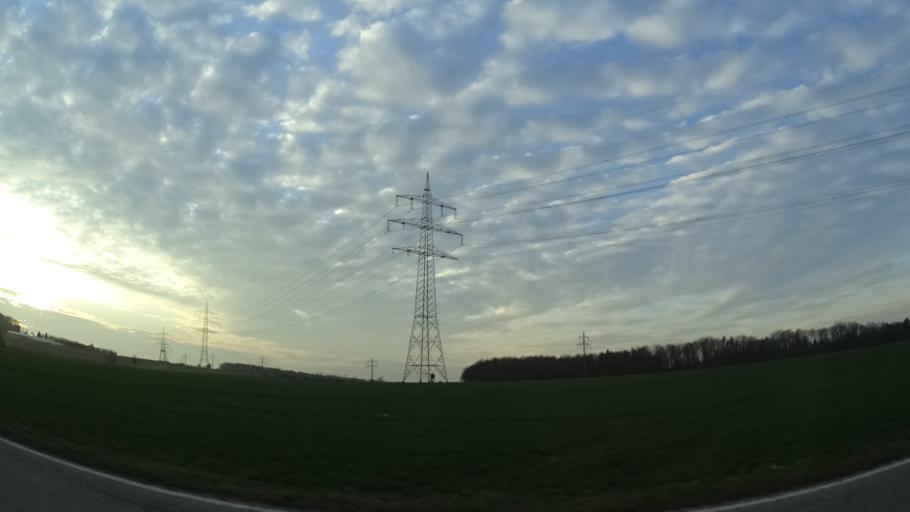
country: DE
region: Baden-Wuerttemberg
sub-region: Regierungsbezirk Stuttgart
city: Hemmingen
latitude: 48.8939
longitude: 9.0099
